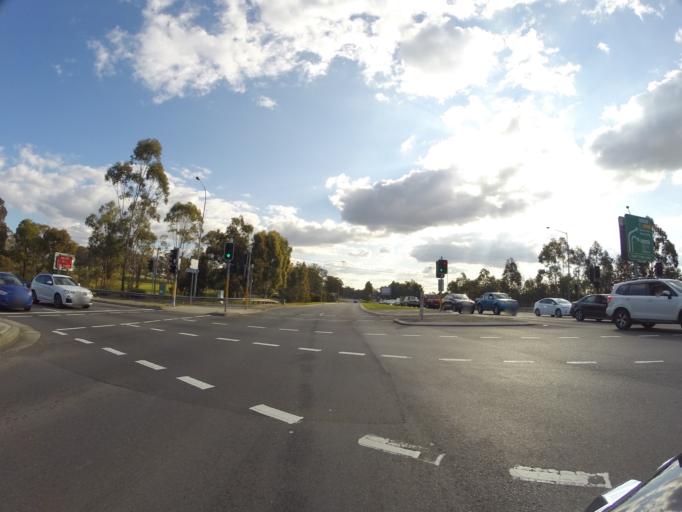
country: AU
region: New South Wales
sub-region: Campbelltown Municipality
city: Glenfield
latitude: -33.9568
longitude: 150.8757
